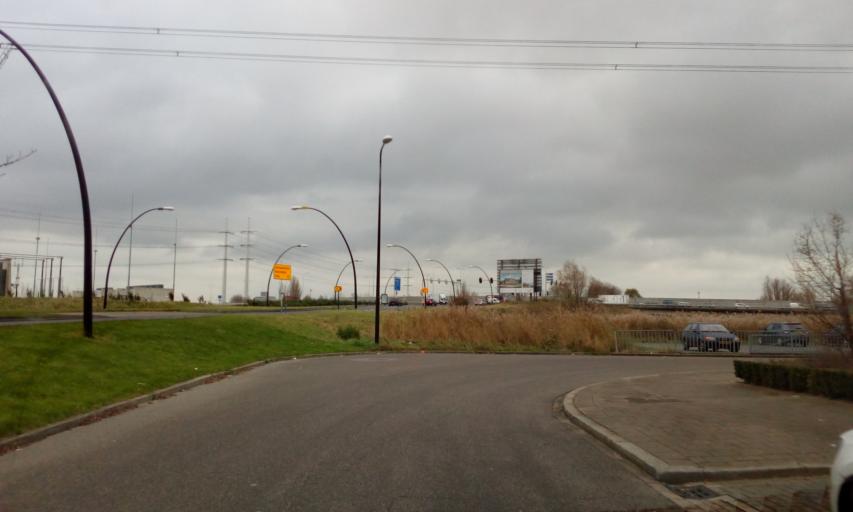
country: NL
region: South Holland
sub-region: Gemeente Rijswijk
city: Rijswijk
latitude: 52.0163
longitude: 4.3041
